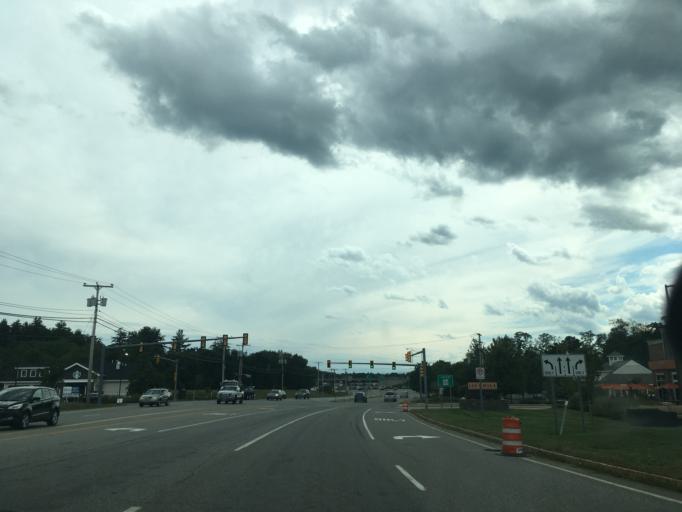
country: US
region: New Hampshire
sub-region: Rockingham County
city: Exeter
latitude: 42.9973
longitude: -70.9239
